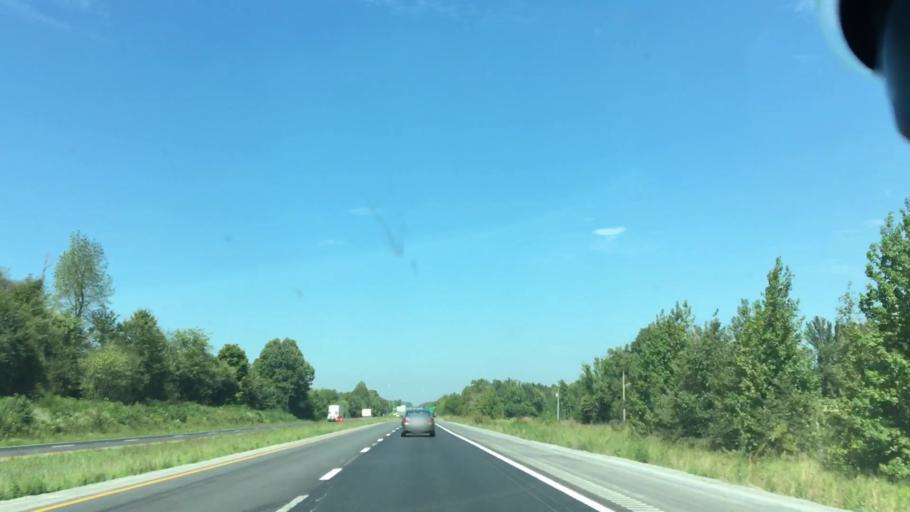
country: US
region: Kentucky
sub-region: Hopkins County
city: Nortonville
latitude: 37.2367
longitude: -87.4466
